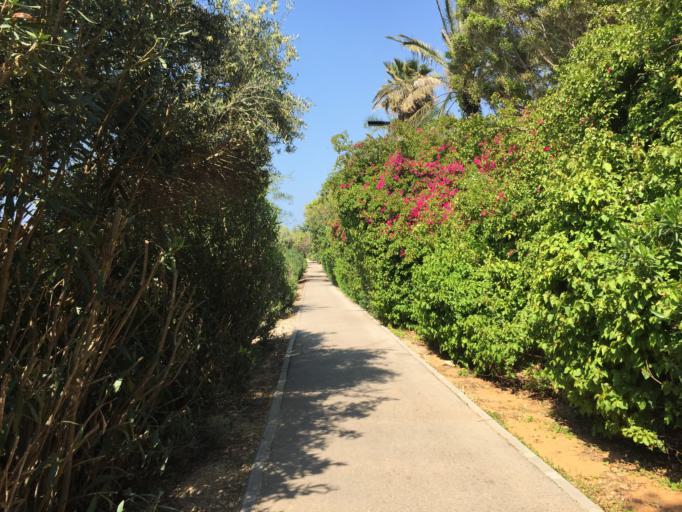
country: IL
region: Haifa
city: Qesarya
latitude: 32.4935
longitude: 34.9042
